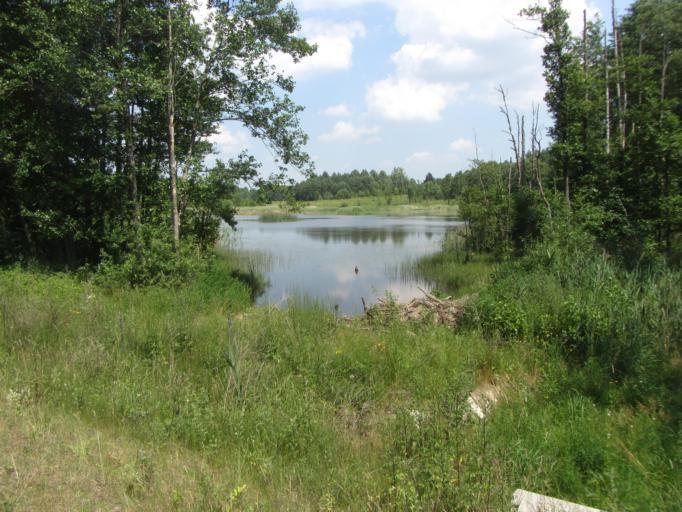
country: LT
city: Lazdijai
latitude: 54.2002
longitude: 23.4144
